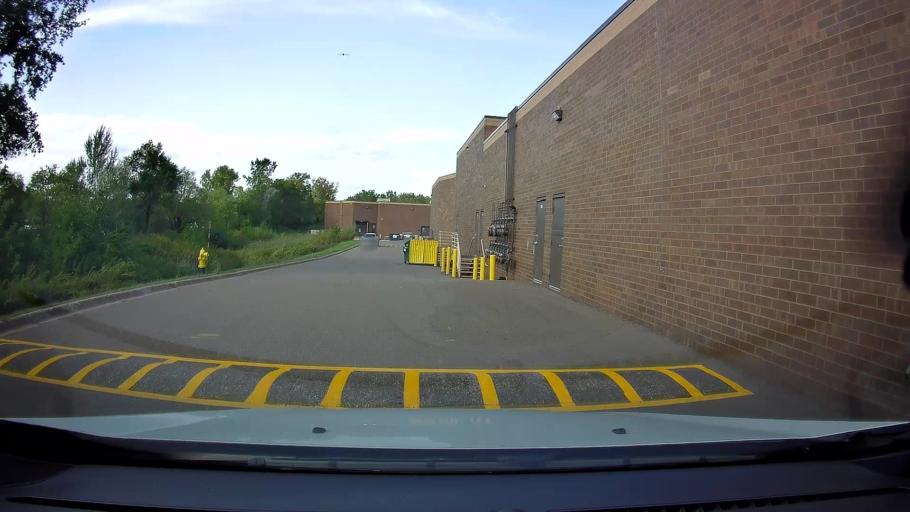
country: US
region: Minnesota
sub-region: Ramsey County
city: Roseville
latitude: 45.0238
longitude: -93.1708
